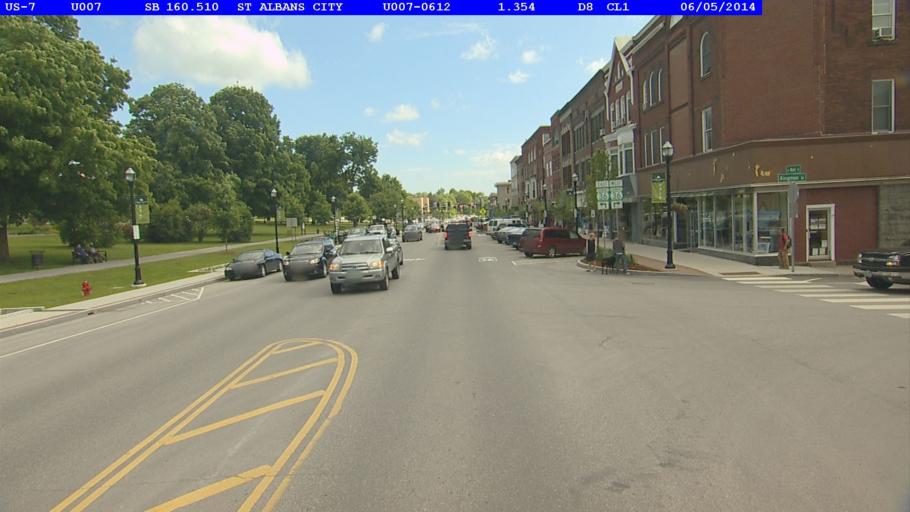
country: US
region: Vermont
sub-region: Franklin County
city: Saint Albans
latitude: 44.8123
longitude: -73.0832
